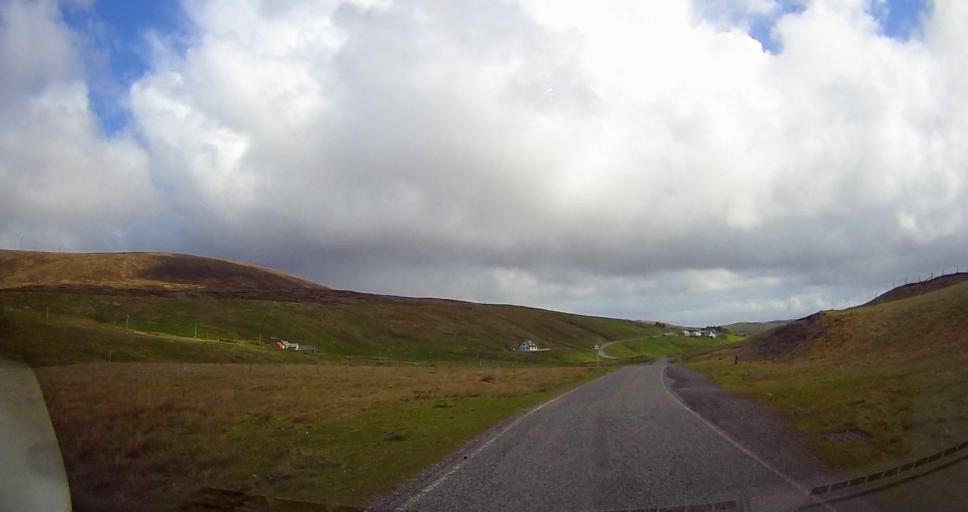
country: GB
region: Scotland
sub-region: Shetland Islands
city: Lerwick
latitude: 60.5210
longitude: -1.3769
